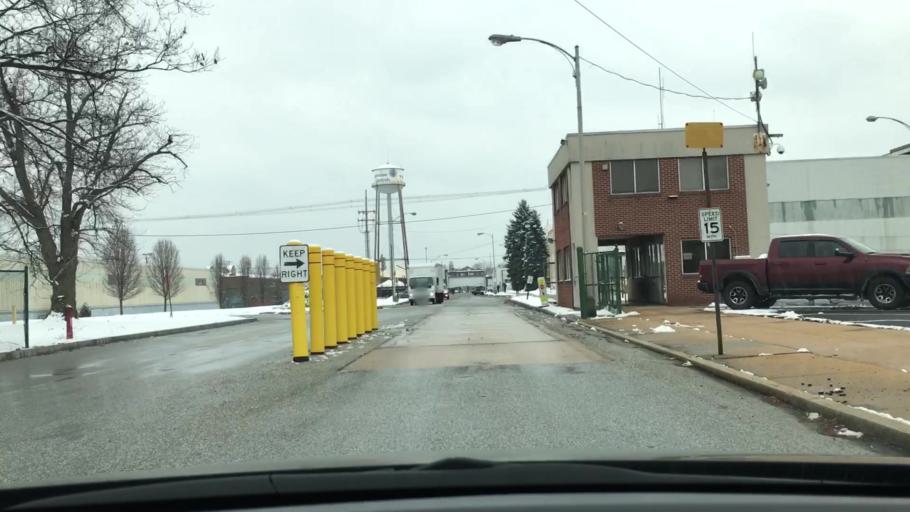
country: US
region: Pennsylvania
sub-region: York County
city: West York
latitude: 39.9489
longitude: -76.7423
